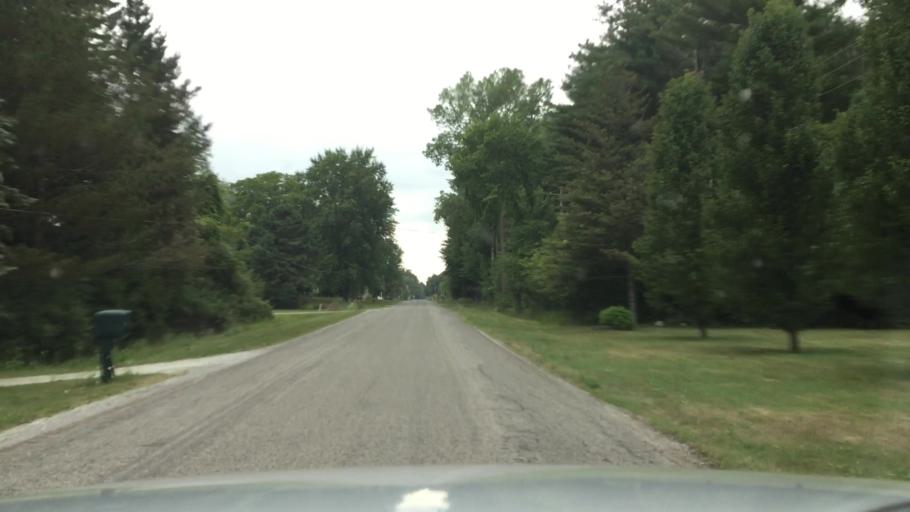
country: US
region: Michigan
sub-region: Saginaw County
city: Birch Run
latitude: 43.3071
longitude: -83.8058
